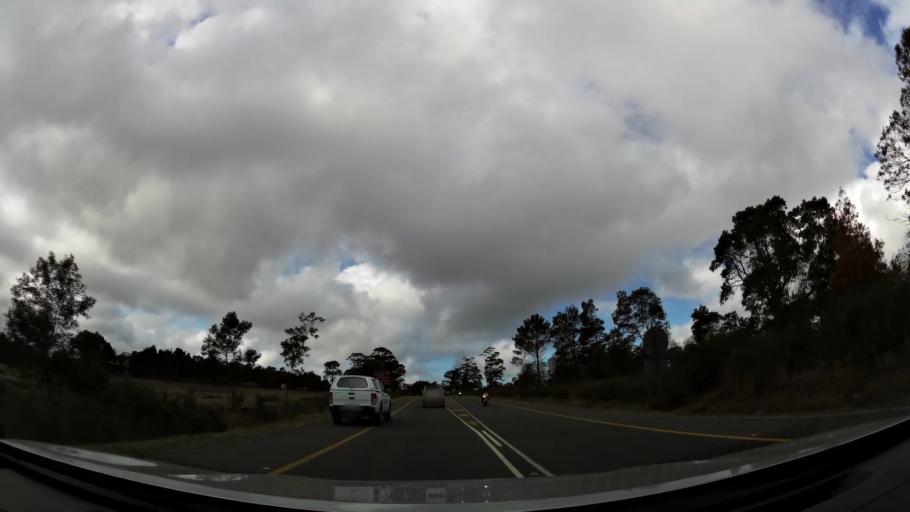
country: ZA
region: Western Cape
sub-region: Eden District Municipality
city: Plettenberg Bay
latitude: -34.0439
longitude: 23.2630
